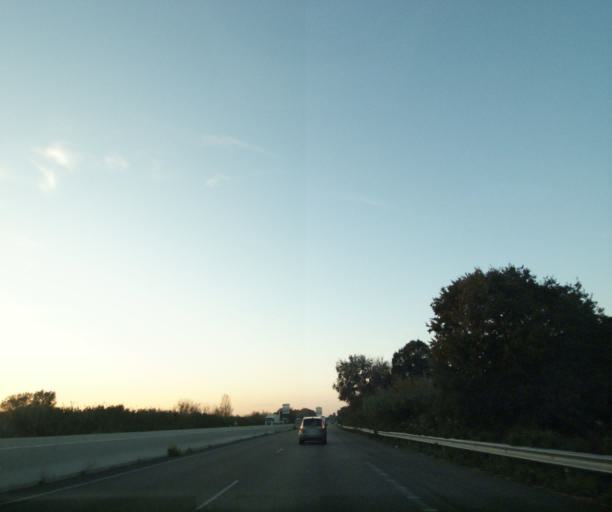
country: FR
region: Provence-Alpes-Cote d'Azur
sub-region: Departement des Bouches-du-Rhone
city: Saint-Martin-de-Crau
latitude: 43.6333
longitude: 4.7417
